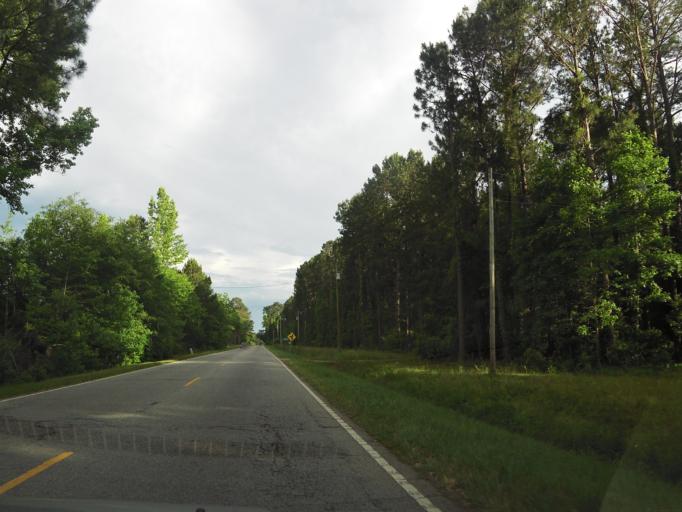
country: US
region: South Carolina
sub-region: Jasper County
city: Ridgeland
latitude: 32.5339
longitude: -81.1556
